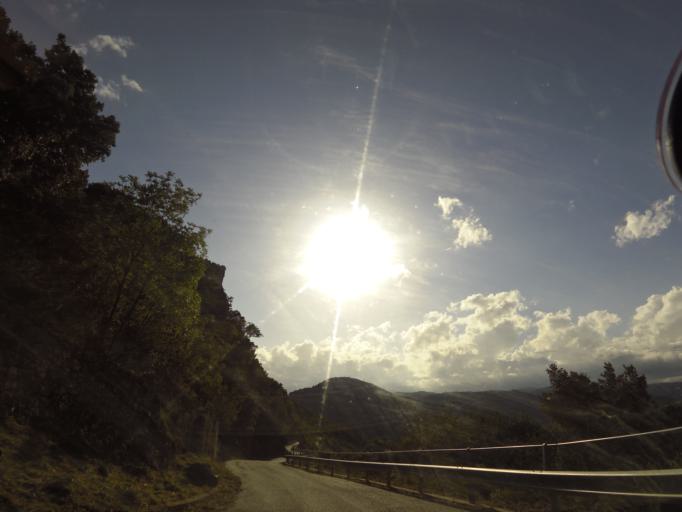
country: IT
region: Calabria
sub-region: Provincia di Reggio Calabria
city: Pazzano
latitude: 38.4658
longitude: 16.4381
